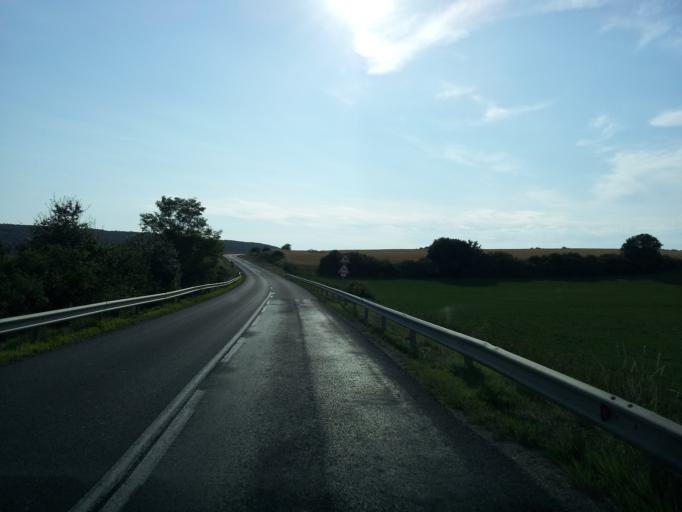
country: HU
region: Veszprem
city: Urkut
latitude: 46.9912
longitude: 17.6767
